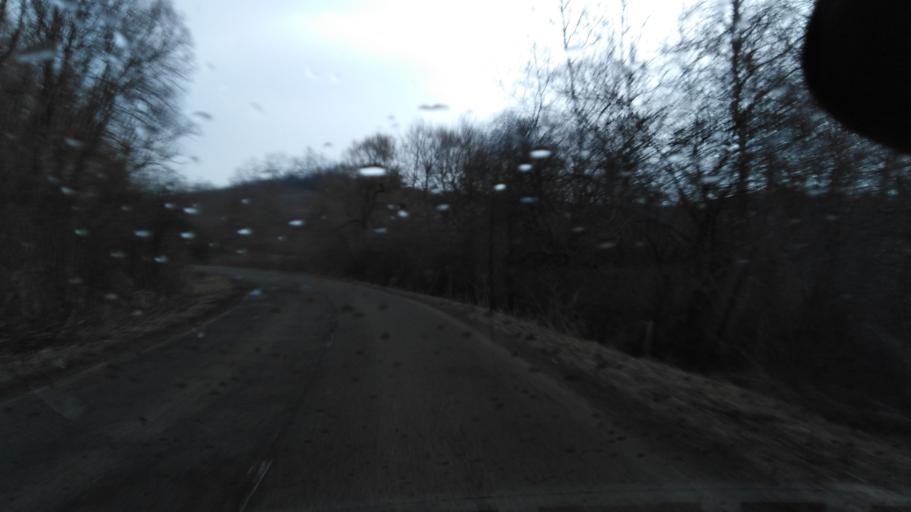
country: HU
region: Nograd
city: Salgotarjan
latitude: 48.0504
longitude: 19.7732
